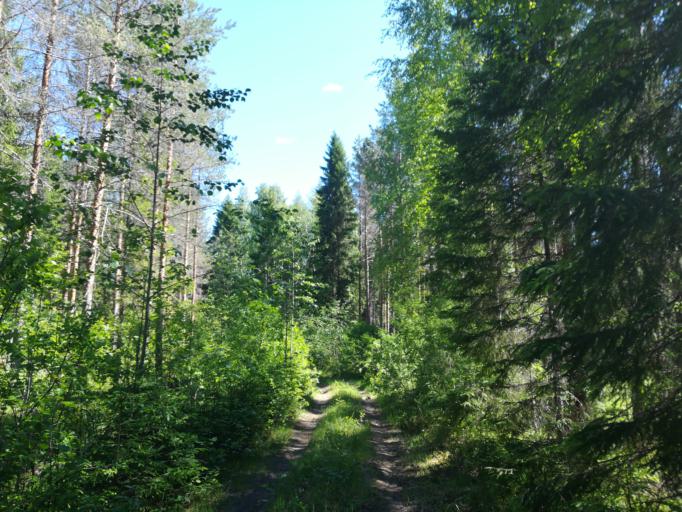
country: FI
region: Southern Savonia
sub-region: Mikkeli
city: Puumala
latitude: 61.6161
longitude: 28.1627
